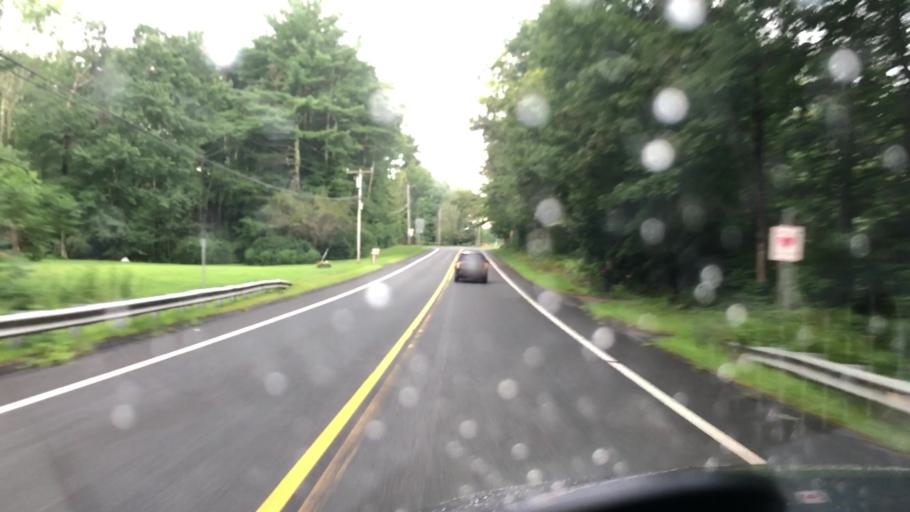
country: US
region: Massachusetts
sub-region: Hampshire County
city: Westhampton
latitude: 42.2908
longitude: -72.7396
